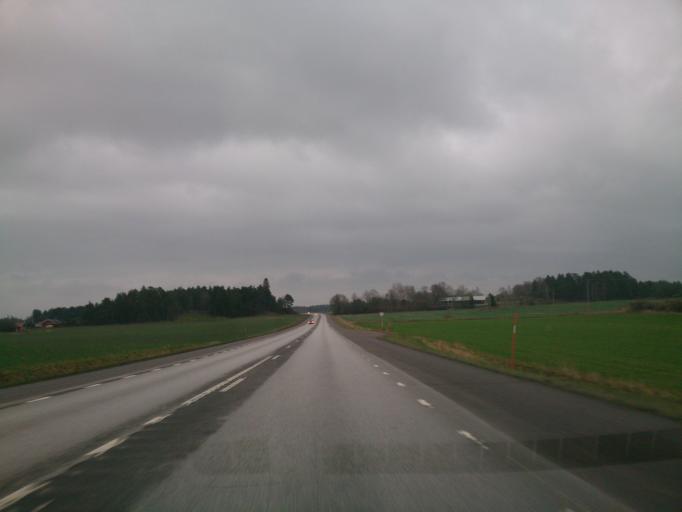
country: SE
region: OEstergoetland
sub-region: Norrkopings Kommun
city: Kimstad
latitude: 58.4783
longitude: 15.9225
